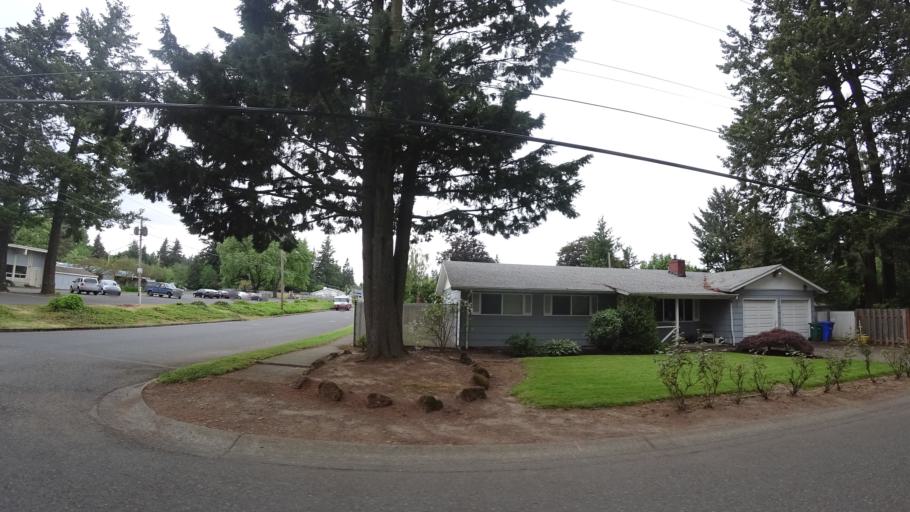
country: US
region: Oregon
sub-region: Multnomah County
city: Lents
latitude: 45.5103
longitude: -122.5196
